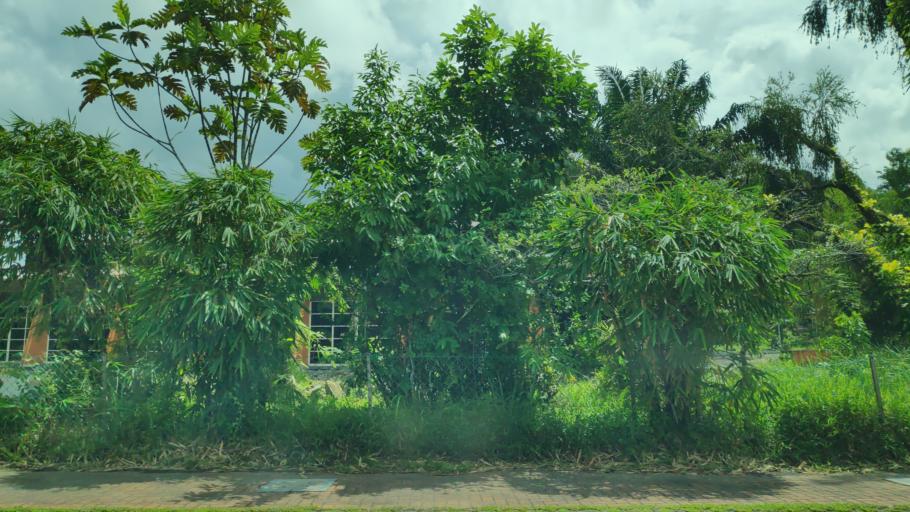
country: MY
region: Sarawak
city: Kuching
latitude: 1.5448
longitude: 110.3446
